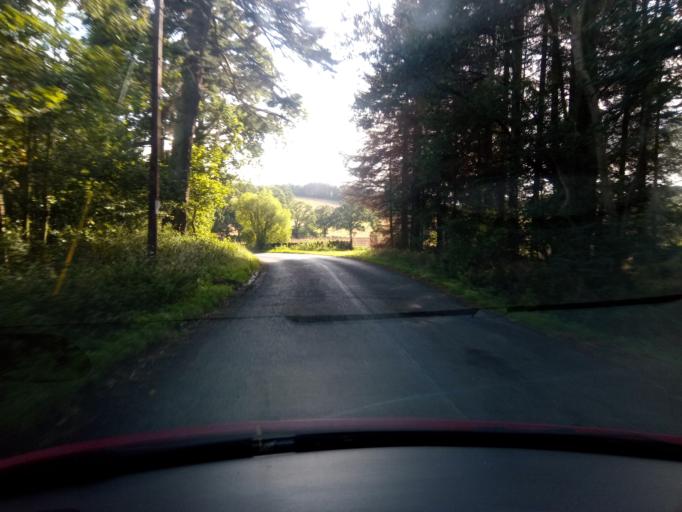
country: GB
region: Scotland
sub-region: The Scottish Borders
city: Kelso
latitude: 55.5580
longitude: -2.3272
